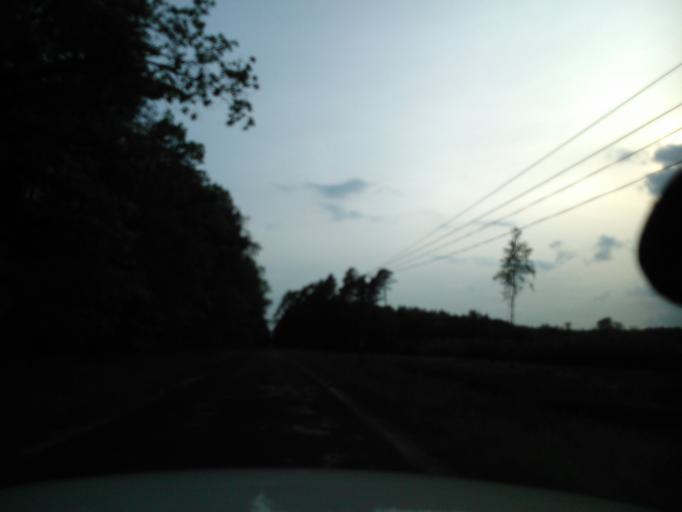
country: PL
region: Kujawsko-Pomorskie
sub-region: Powiat golubsko-dobrzynski
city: Golub-Dobrzyn
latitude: 53.1438
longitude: 19.1237
